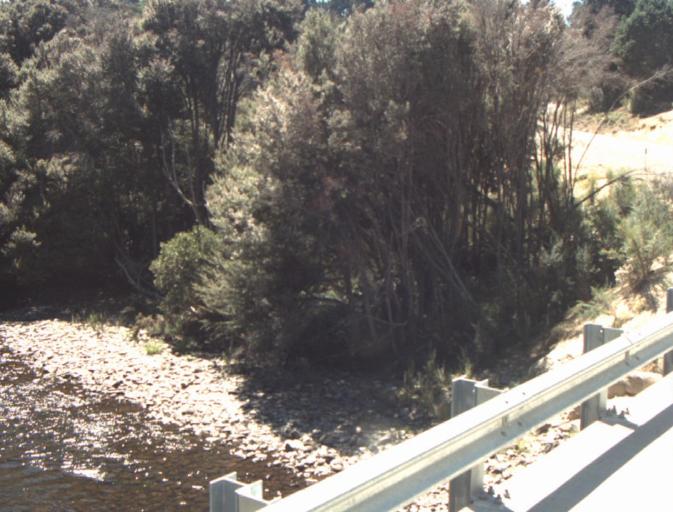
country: AU
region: Tasmania
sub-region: Dorset
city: Scottsdale
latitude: -41.3170
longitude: 147.4649
